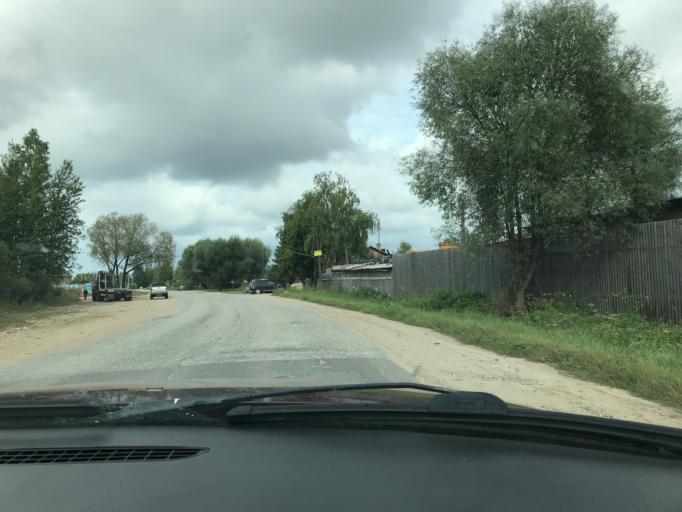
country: RU
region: Kaluga
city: Maloyaroslavets
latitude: 54.9852
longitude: 36.4716
